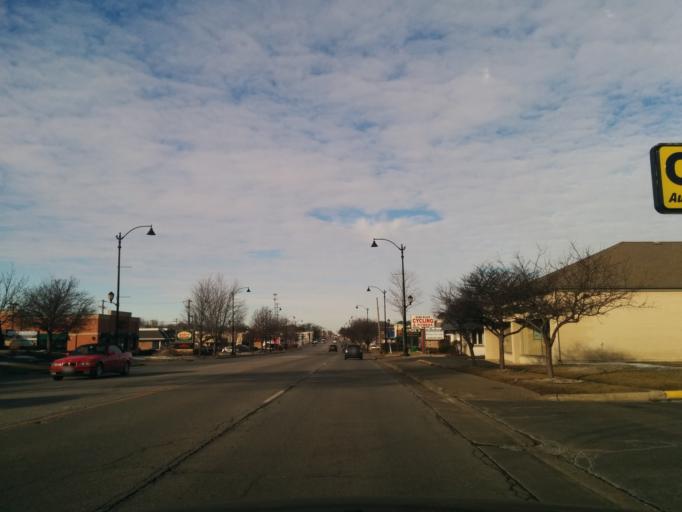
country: US
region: Illinois
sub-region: DuPage County
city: Glen Ellyn
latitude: 41.8595
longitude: -88.0687
